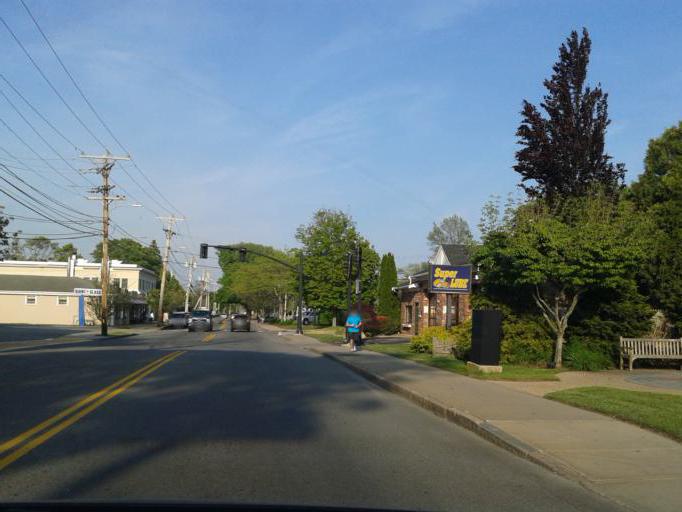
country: US
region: Massachusetts
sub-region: Barnstable County
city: Falmouth
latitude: 41.5522
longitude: -70.6115
